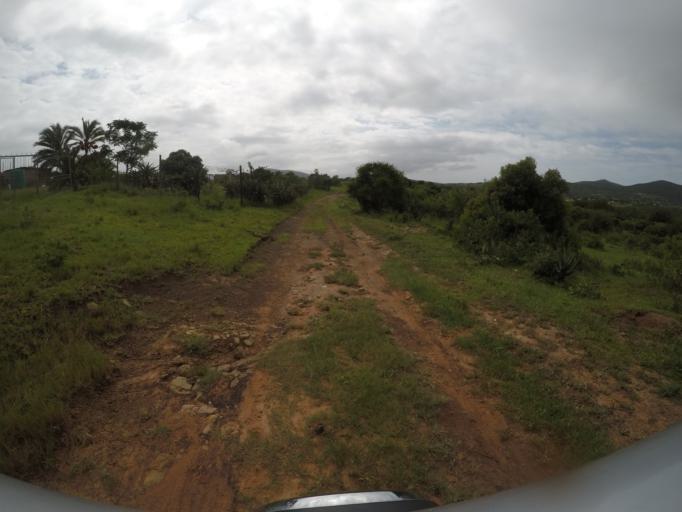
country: ZA
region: KwaZulu-Natal
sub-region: uThungulu District Municipality
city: Empangeni
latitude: -28.6166
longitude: 31.8465
